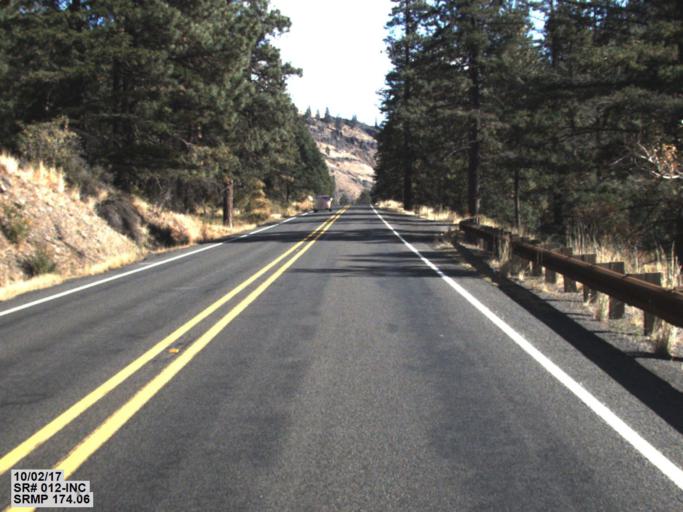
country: US
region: Washington
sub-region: Yakima County
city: Tieton
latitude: 46.6767
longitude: -120.9668
